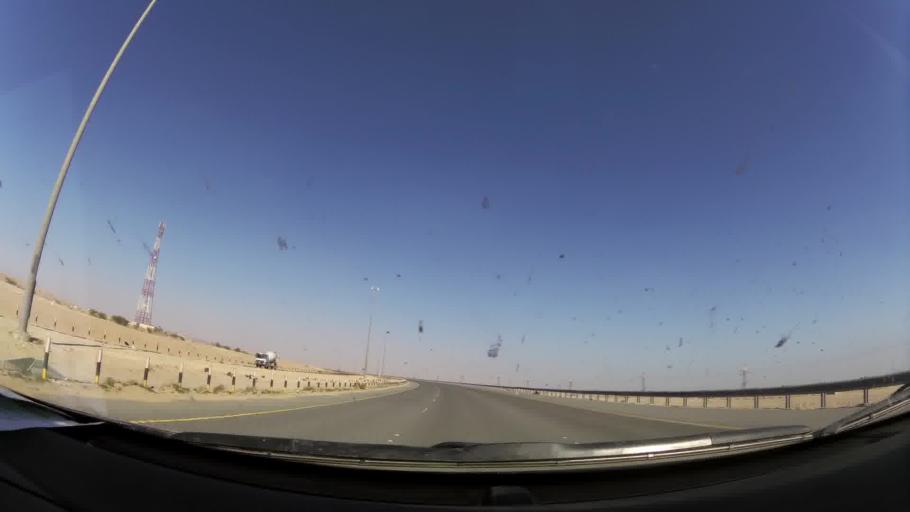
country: KW
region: Muhafazat al Jahra'
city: Al Jahra'
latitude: 29.4477
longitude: 47.7540
